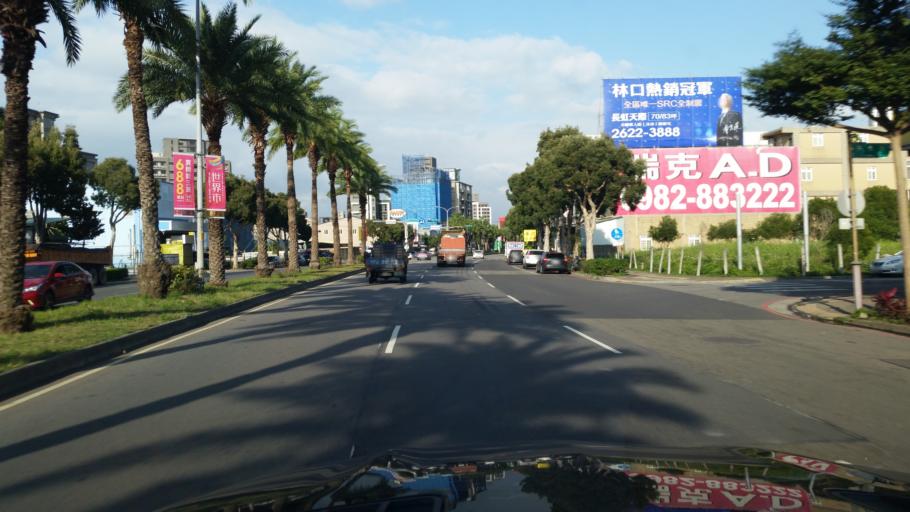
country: TW
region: Taiwan
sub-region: Taoyuan
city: Taoyuan
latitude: 25.0694
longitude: 121.3568
